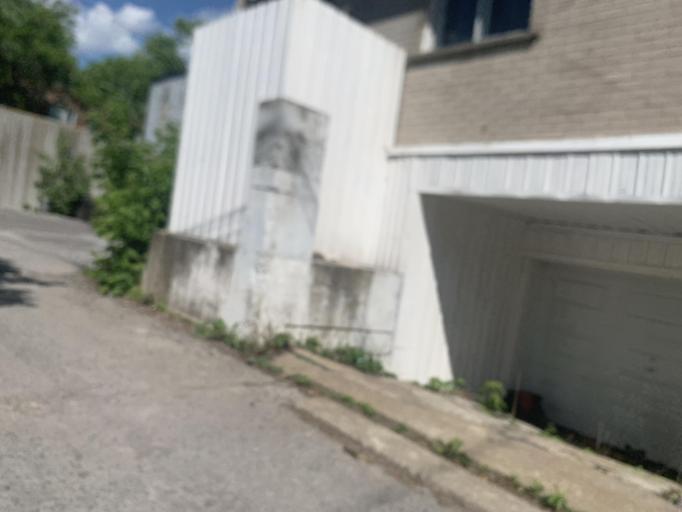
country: CA
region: Quebec
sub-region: Montreal
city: Montreal
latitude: 45.5450
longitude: -73.5883
